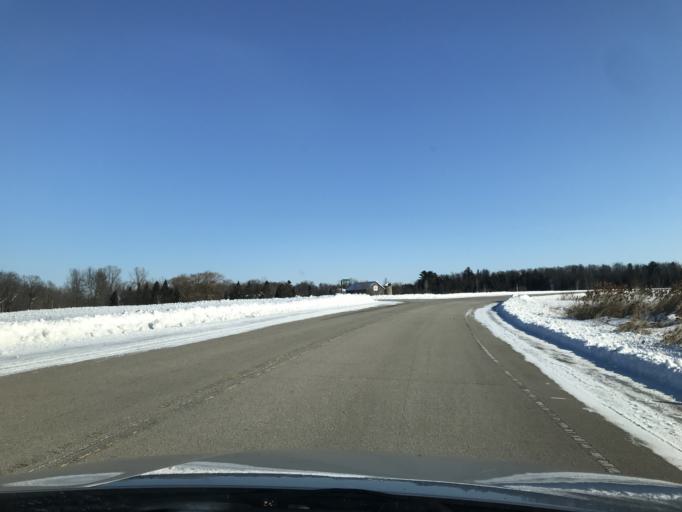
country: US
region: Wisconsin
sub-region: Oconto County
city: Oconto Falls
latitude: 44.9694
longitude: -88.0454
